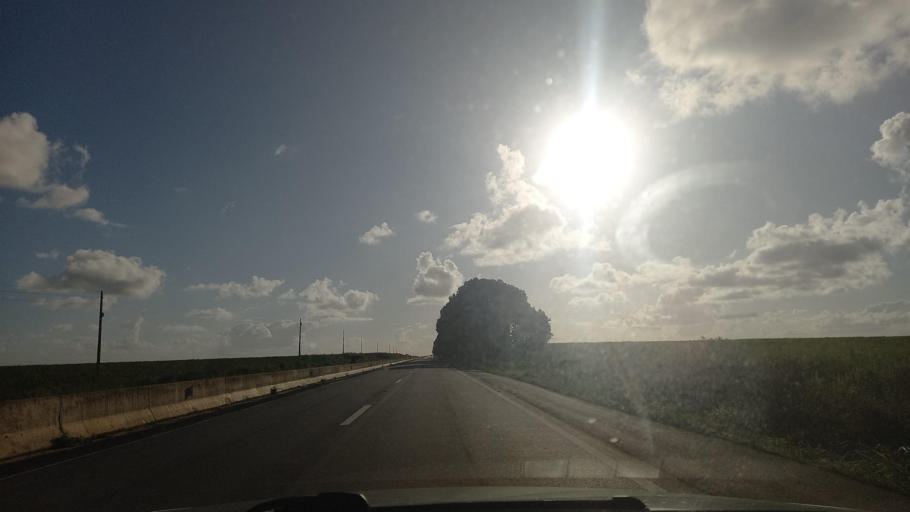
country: BR
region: Alagoas
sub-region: Sao Miguel Dos Campos
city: Sao Miguel dos Campos
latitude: -9.8015
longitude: -36.1524
